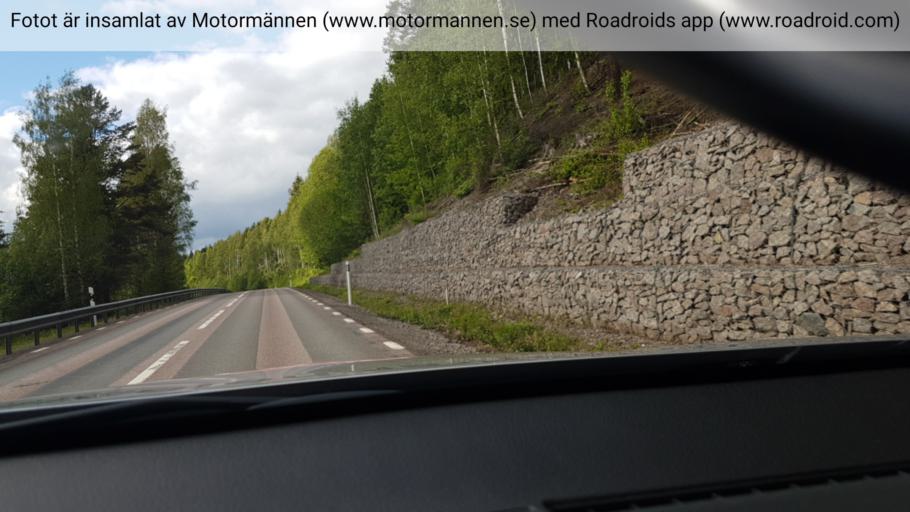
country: SE
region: Vaermland
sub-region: Torsby Kommun
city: Torsby
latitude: 60.5493
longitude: 13.1140
